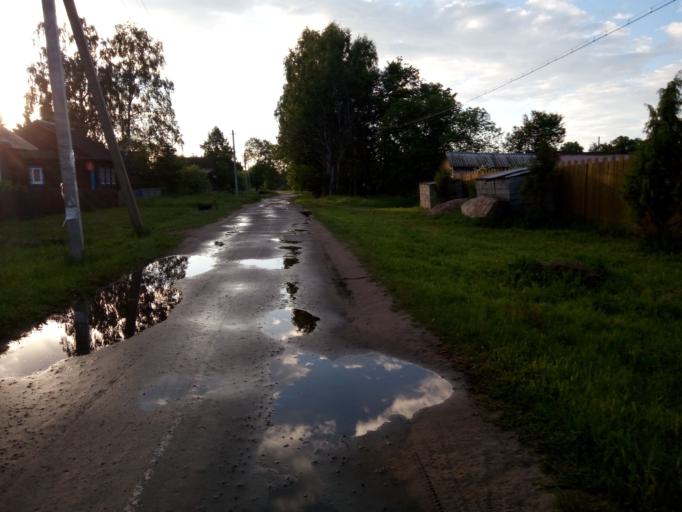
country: RU
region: Nizjnij Novgorod
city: Voskresenskoye
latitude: 56.7761
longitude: 45.5414
